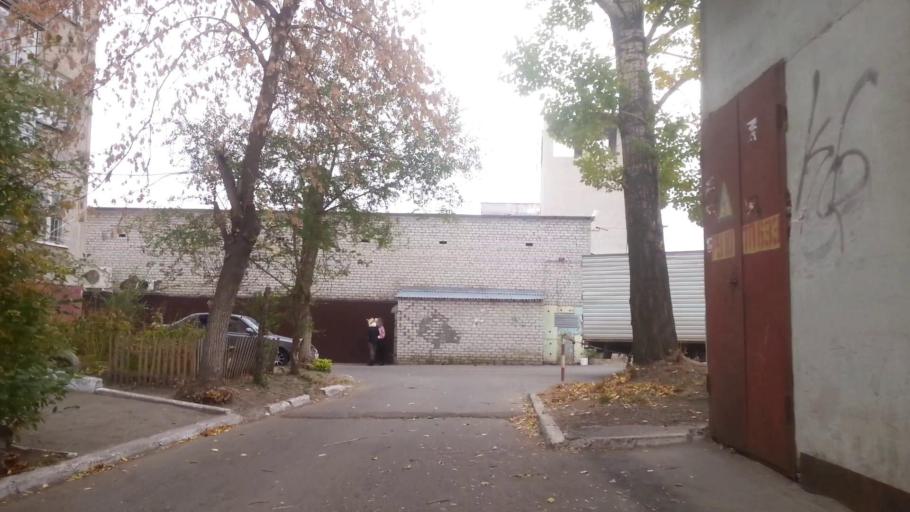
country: RU
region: Altai Krai
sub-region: Gorod Barnaulskiy
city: Barnaul
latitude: 53.3666
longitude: 83.7098
